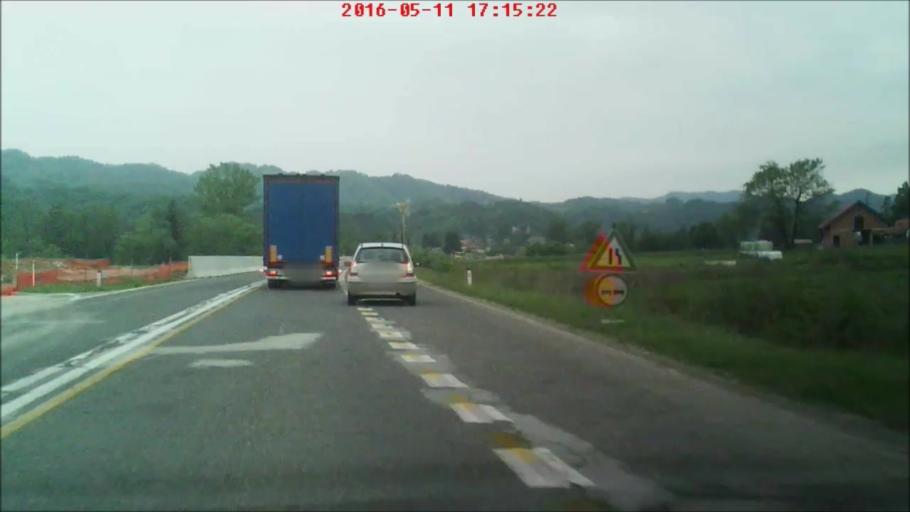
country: SI
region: Podlehnik
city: Podlehnik
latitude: 46.3267
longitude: 15.8800
